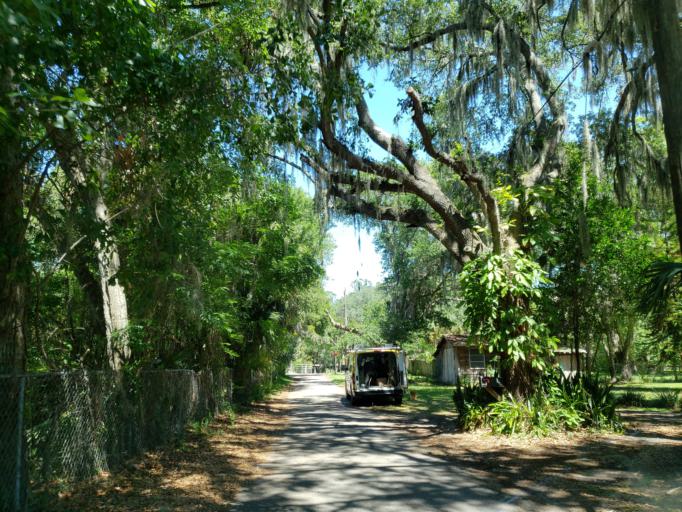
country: US
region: Florida
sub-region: Hillsborough County
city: Riverview
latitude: 27.8618
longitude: -82.3193
